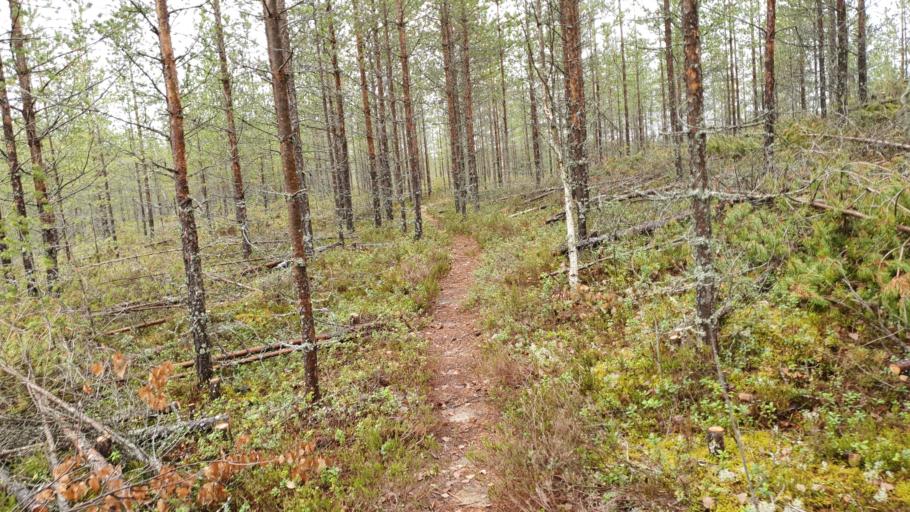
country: FI
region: Kainuu
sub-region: Kehys-Kainuu
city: Kuhmo
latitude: 64.1507
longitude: 29.3979
